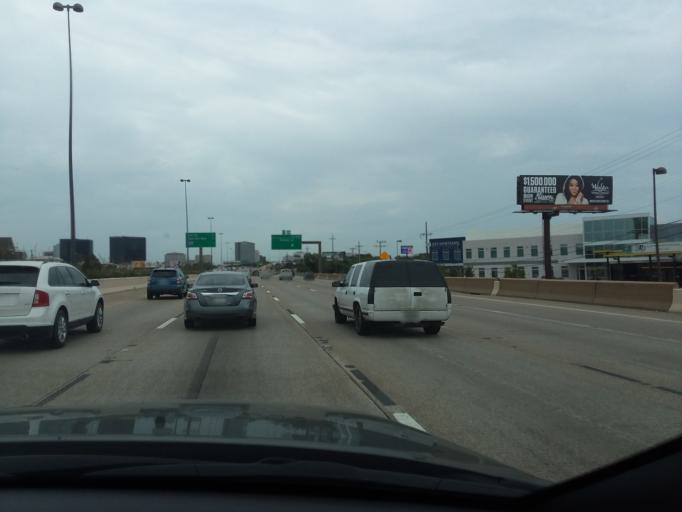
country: US
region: Texas
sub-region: Dallas County
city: Richardson
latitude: 32.9027
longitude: -96.7688
